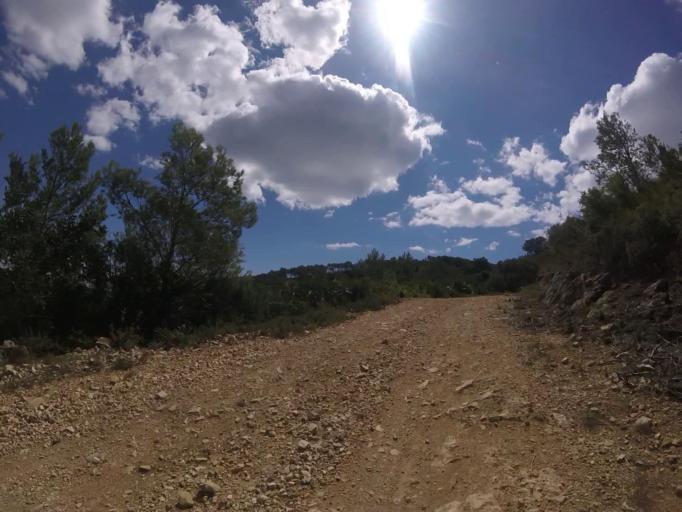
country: ES
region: Valencia
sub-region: Provincia de Castello
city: Santa Magdalena de Pulpis
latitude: 40.3091
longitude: 0.3209
